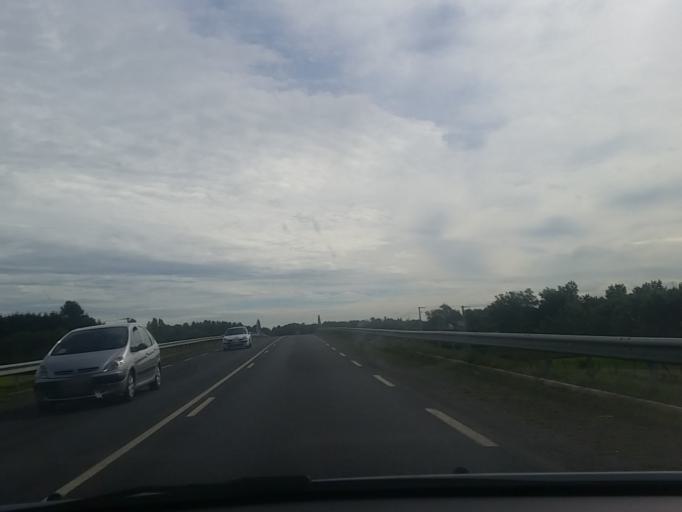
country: FR
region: Pays de la Loire
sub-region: Departement de la Loire-Atlantique
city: Chateaubriant
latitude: 47.7002
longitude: -1.3789
